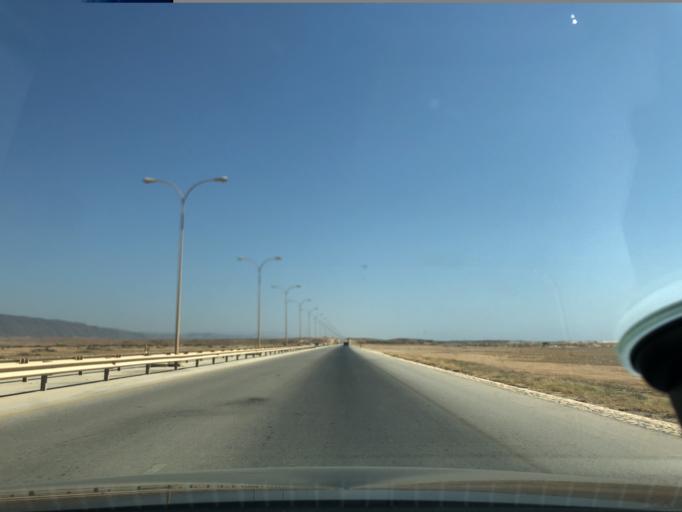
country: OM
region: Zufar
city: Salalah
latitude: 17.0521
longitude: 54.2996
